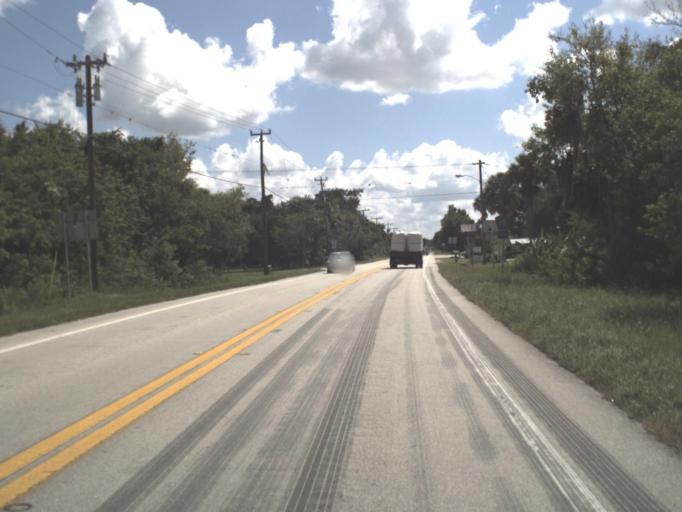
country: US
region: Florida
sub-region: Okeechobee County
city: Taylor Creek
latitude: 27.1488
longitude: -80.6968
